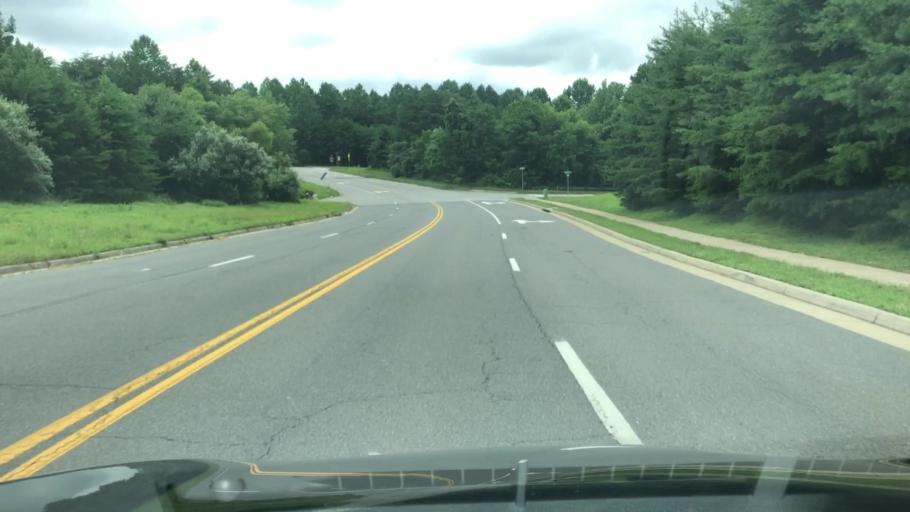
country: US
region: Virginia
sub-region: Stafford County
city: Falmouth
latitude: 38.3644
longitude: -77.5289
